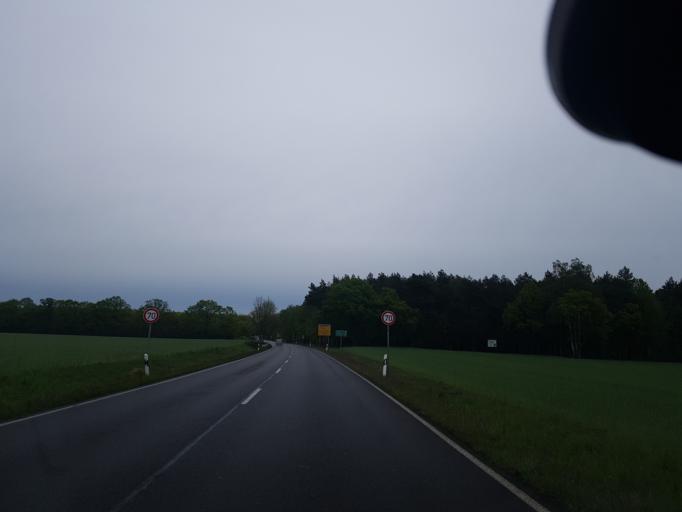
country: DE
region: Brandenburg
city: Neupetershain
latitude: 51.6085
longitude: 14.1357
